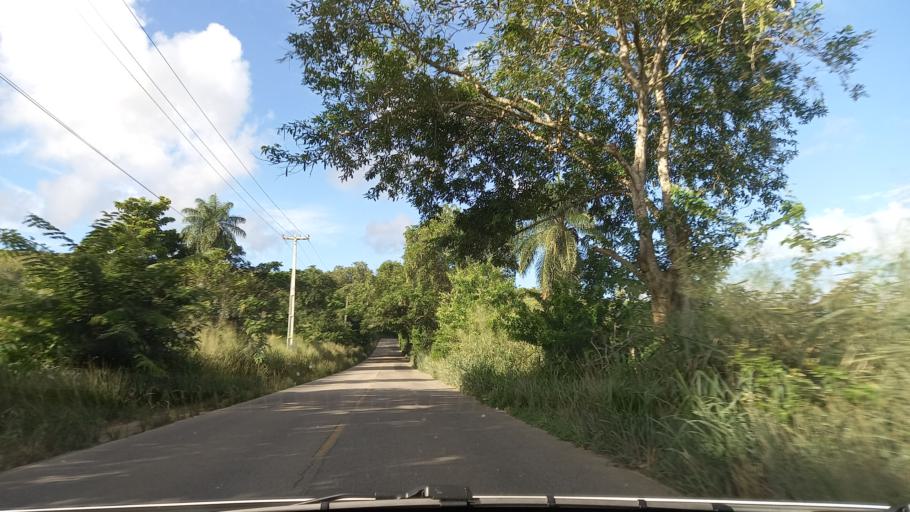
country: BR
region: Pernambuco
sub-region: Rio Formoso
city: Rio Formoso
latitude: -8.6545
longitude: -35.1361
